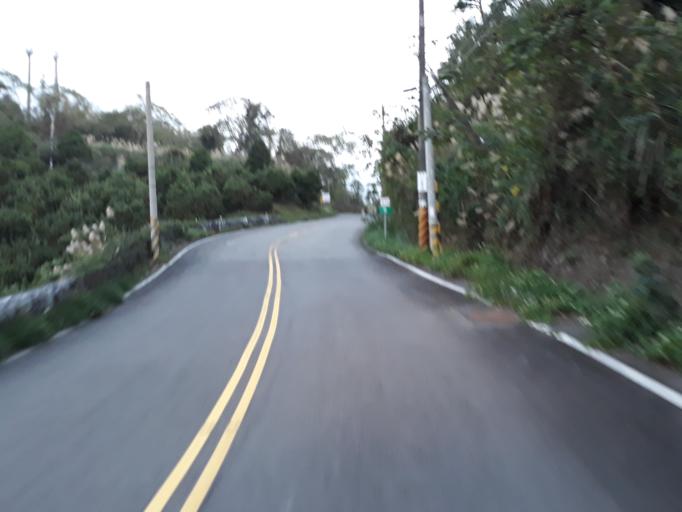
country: TW
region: Taiwan
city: Fengyuan
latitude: 24.3612
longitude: 120.8683
